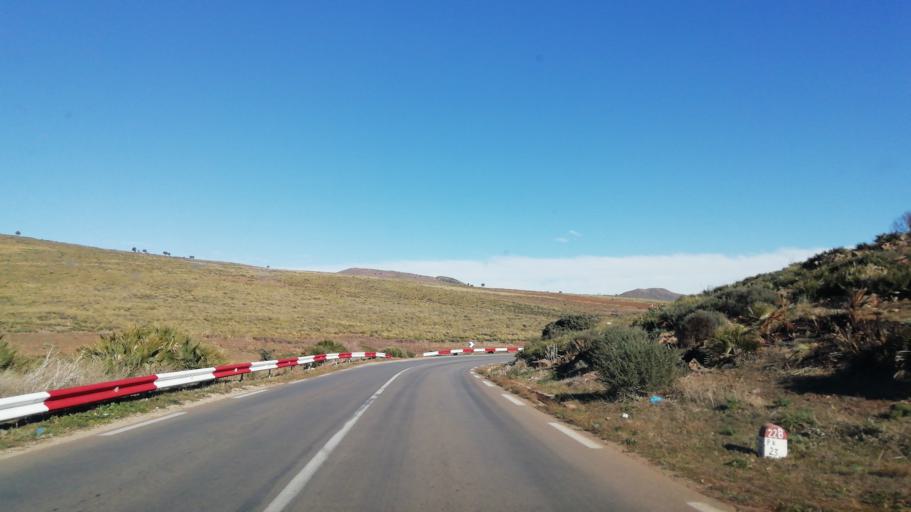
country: DZ
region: Tlemcen
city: Ouled Mimoun
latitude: 34.7709
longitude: -1.1362
